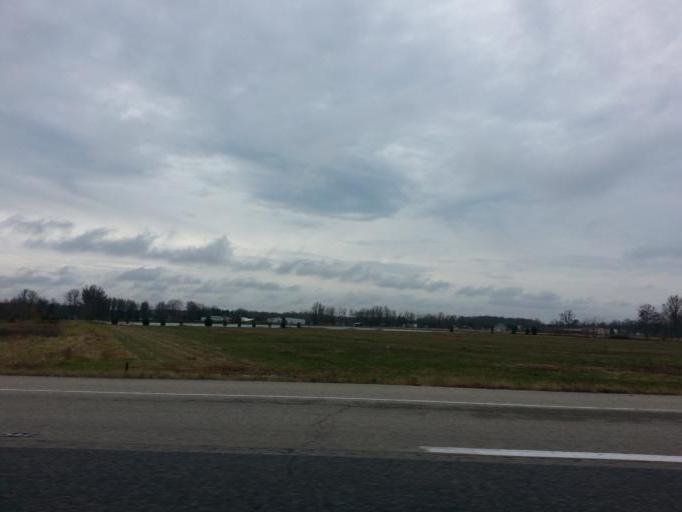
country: US
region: Indiana
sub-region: Ripley County
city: Batesville
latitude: 39.2886
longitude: -85.1701
